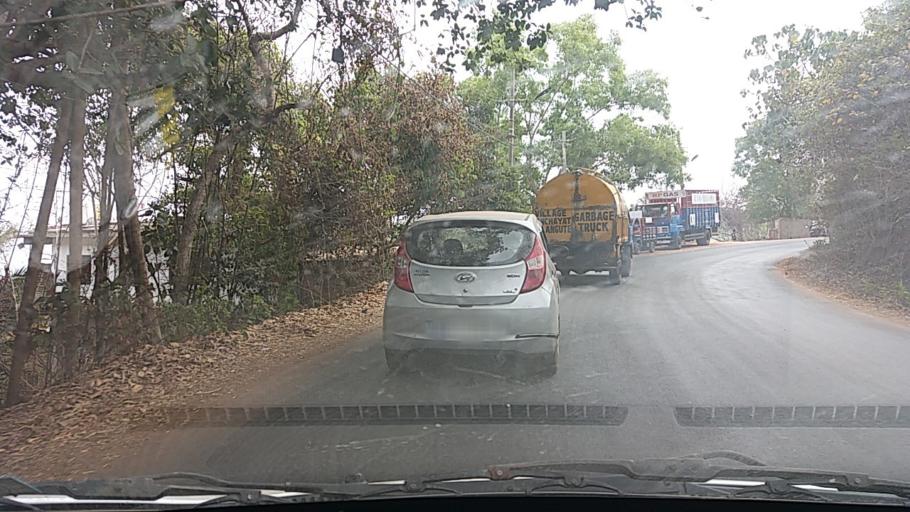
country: IN
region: Goa
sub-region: North Goa
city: Saligao
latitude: 15.5397
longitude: 73.7923
